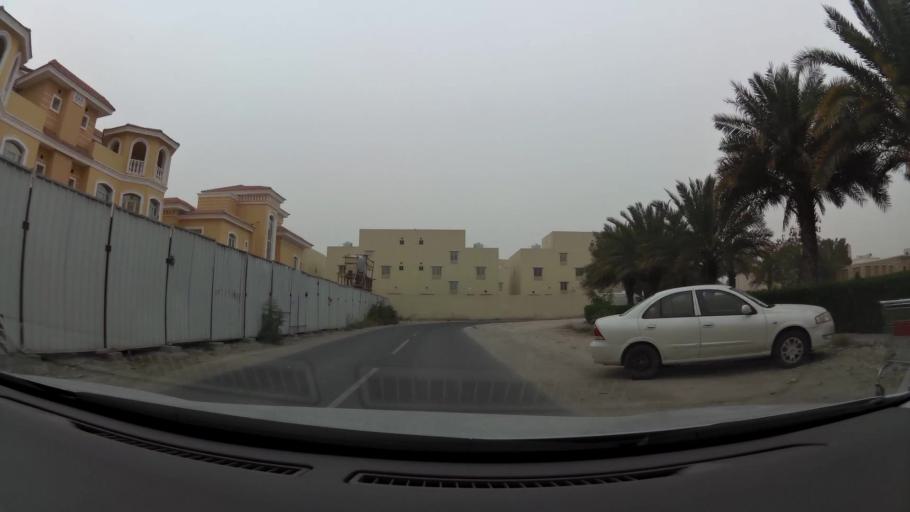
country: QA
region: Baladiyat ad Dawhah
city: Doha
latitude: 25.2471
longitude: 51.4877
